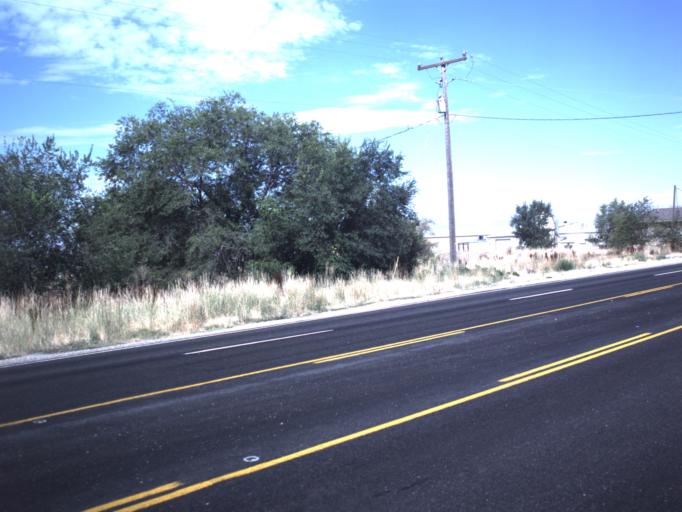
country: US
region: Utah
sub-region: Weber County
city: Pleasant View
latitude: 41.3133
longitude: -112.0107
